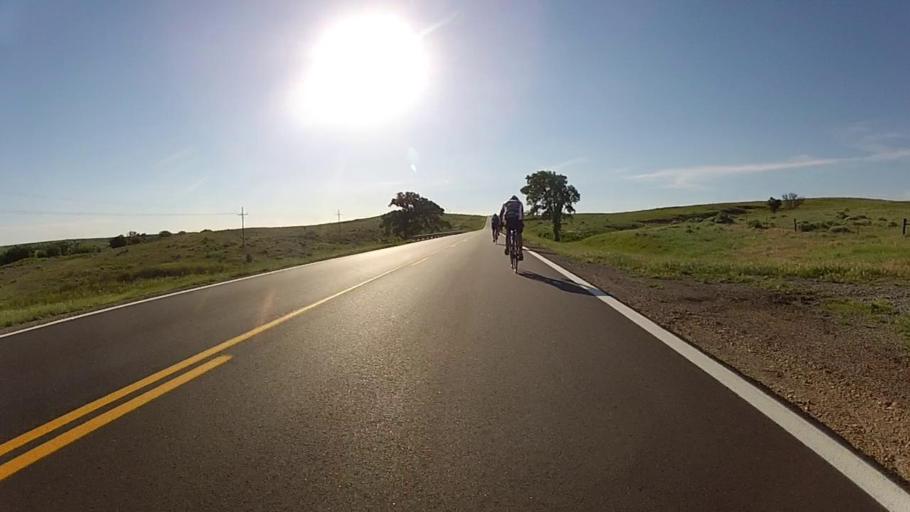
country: US
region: Kansas
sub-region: Comanche County
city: Coldwater
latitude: 37.2807
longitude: -99.0295
